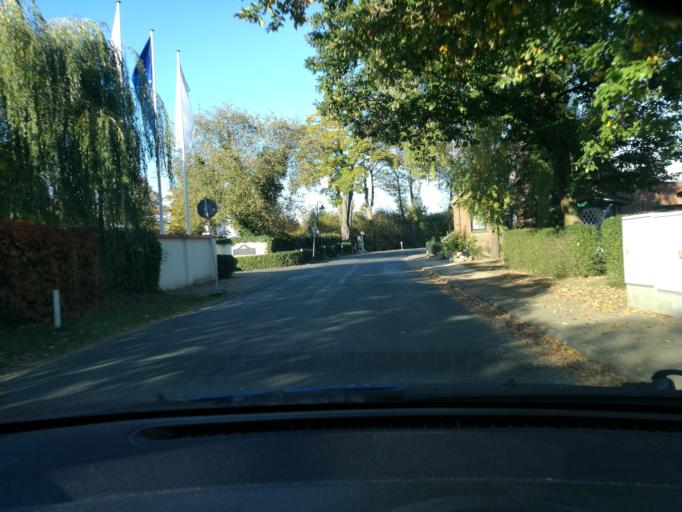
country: DE
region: Lower Saxony
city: Ludersburg
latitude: 53.3218
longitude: 10.5744
